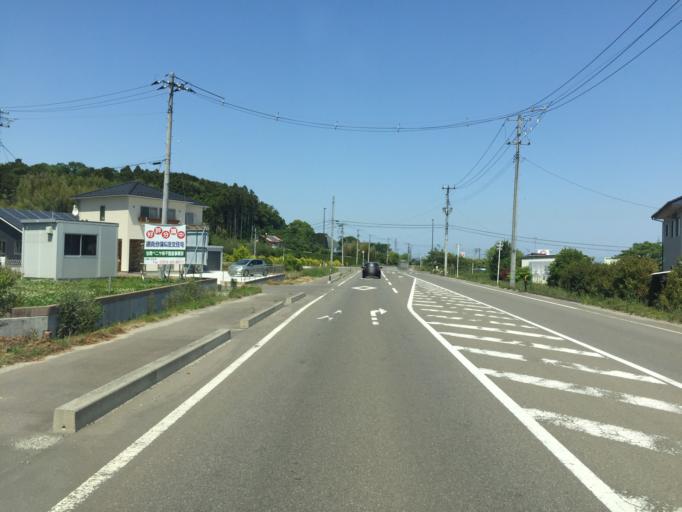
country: JP
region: Miyagi
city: Watari
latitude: 37.9826
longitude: 140.8656
